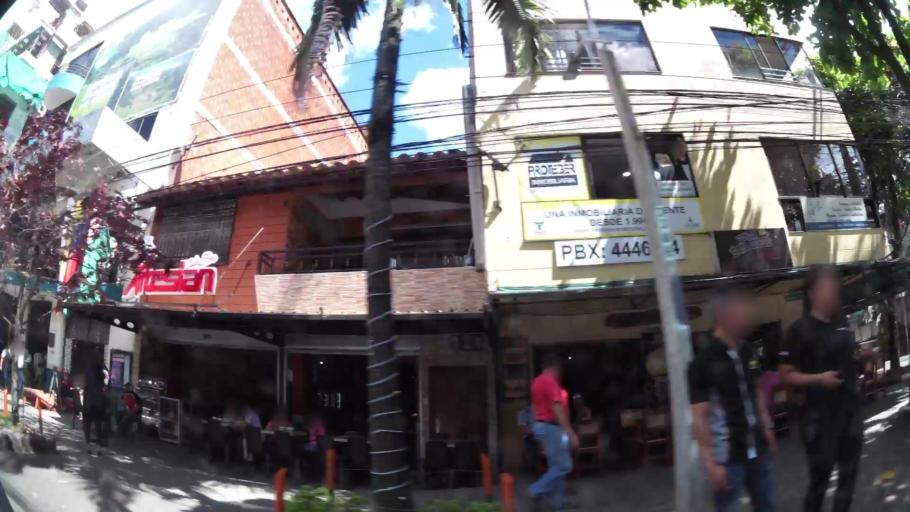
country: CO
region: Antioquia
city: Sabaneta
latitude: 6.1507
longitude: -75.6165
